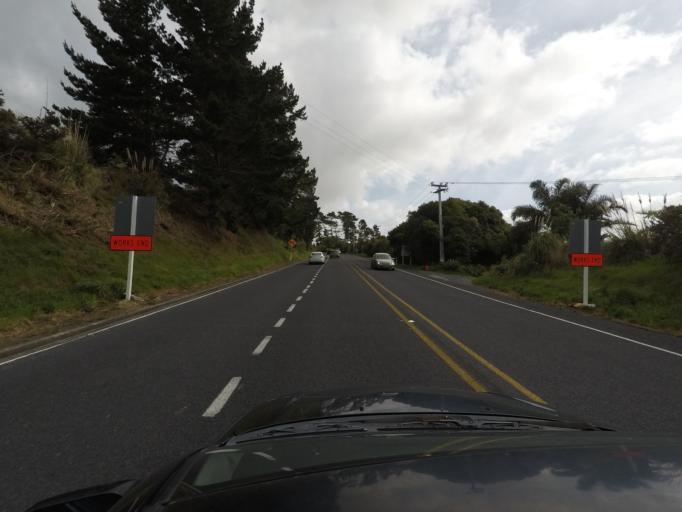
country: NZ
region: Auckland
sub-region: Auckland
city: Pakuranga
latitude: -36.9260
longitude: 174.9359
